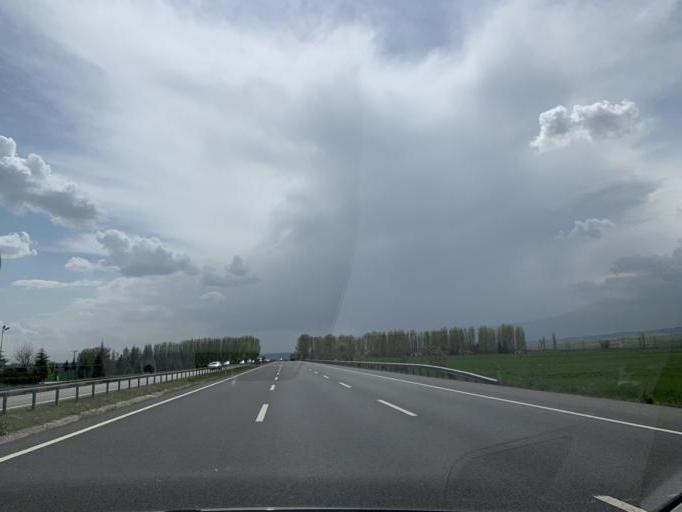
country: TR
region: Ankara
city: Temelli
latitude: 39.6953
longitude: 32.2608
